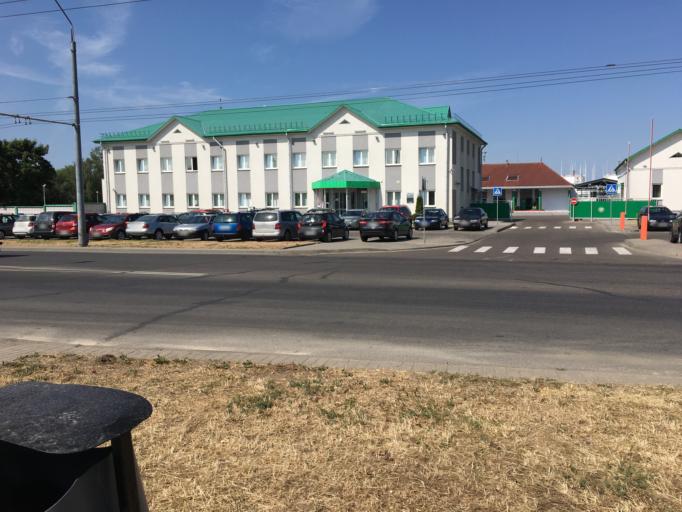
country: BY
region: Grodnenskaya
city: Hrodna
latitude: 53.7086
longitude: 23.8400
